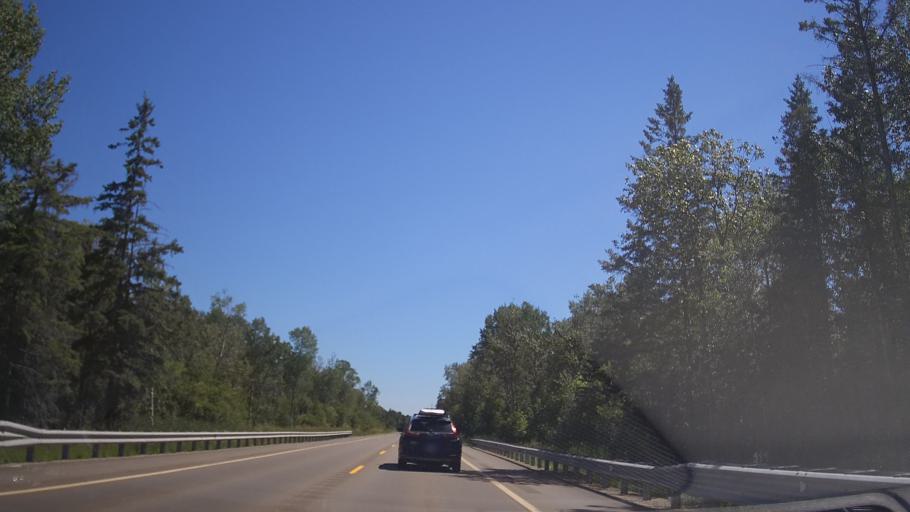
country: US
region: Michigan
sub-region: Cheboygan County
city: Indian River
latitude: 45.6039
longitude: -84.7823
